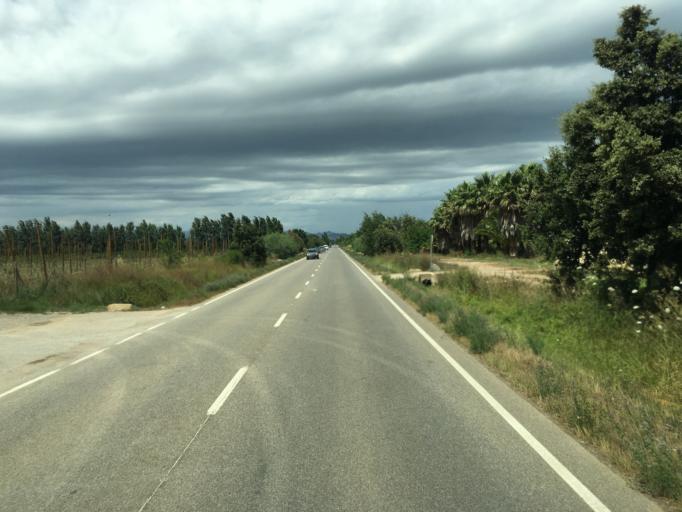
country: ES
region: Catalonia
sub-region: Provincia de Girona
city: Sant Pere Pescador
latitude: 42.2020
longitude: 3.0841
